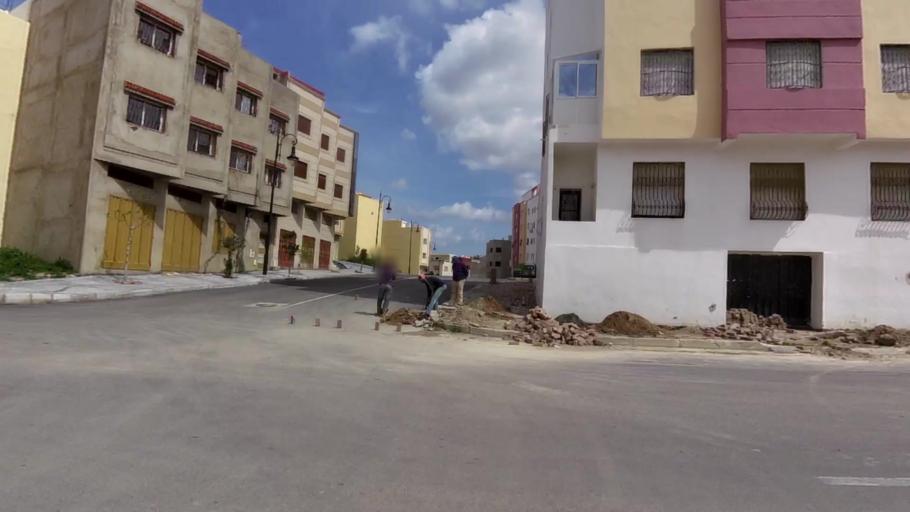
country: MA
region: Tanger-Tetouan
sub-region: Tanger-Assilah
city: Tangier
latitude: 35.7611
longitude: -5.7597
